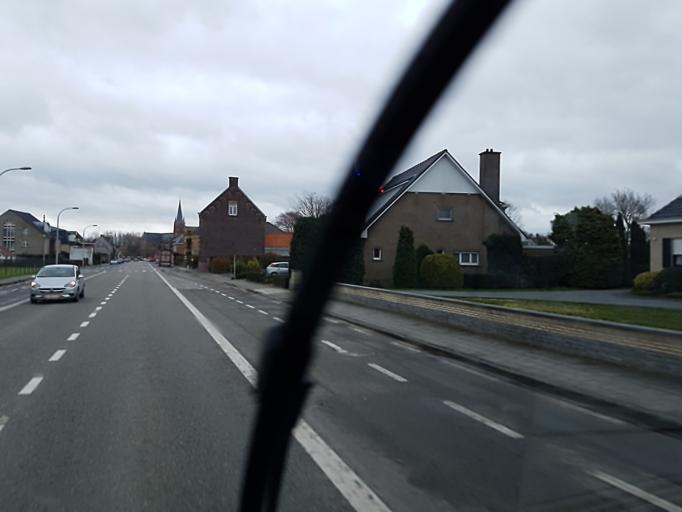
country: BE
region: Flanders
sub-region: Provincie Oost-Vlaanderen
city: De Pinte
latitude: 50.9584
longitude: 3.6362
